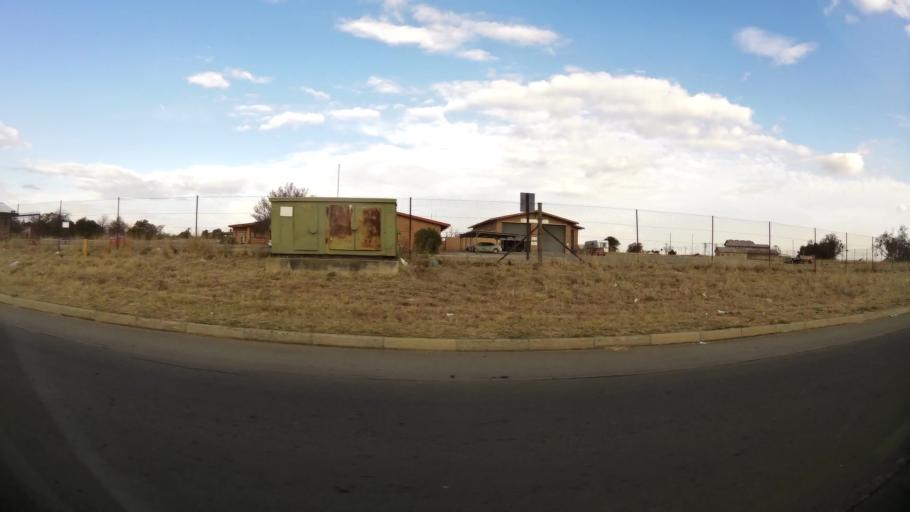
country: ZA
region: Orange Free State
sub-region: Lejweleputswa District Municipality
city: Welkom
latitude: -28.0020
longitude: 26.7372
